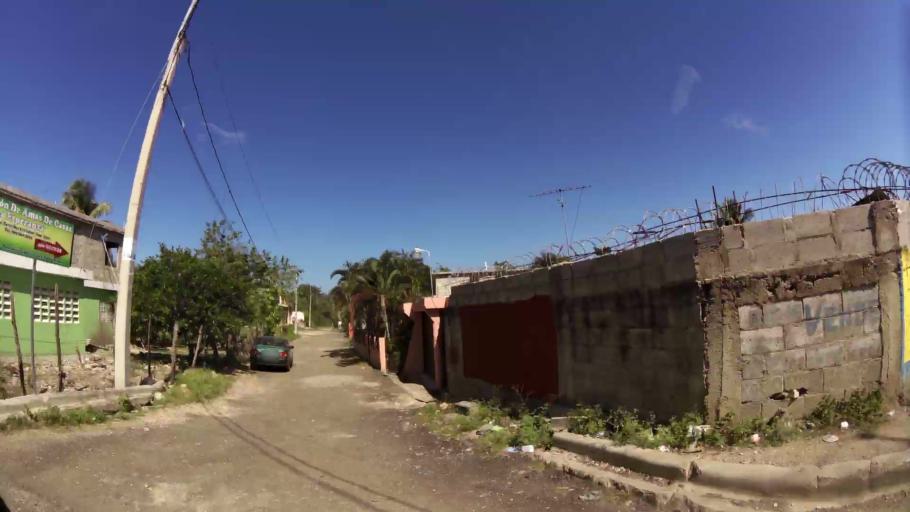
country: DO
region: San Cristobal
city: San Cristobal
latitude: 18.4294
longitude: -70.1337
